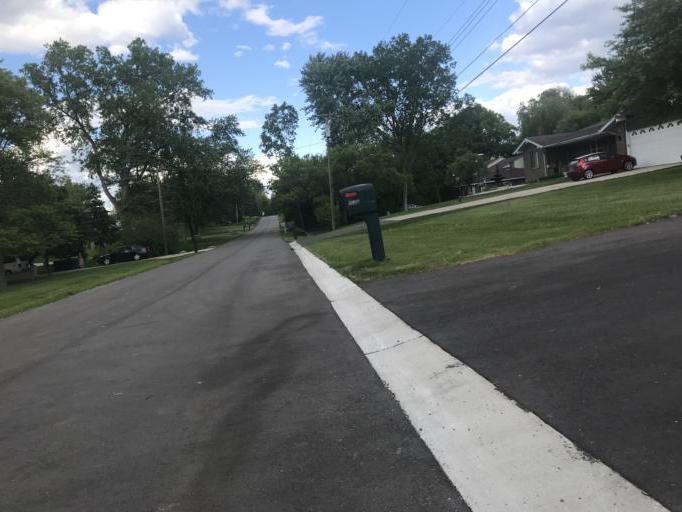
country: US
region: Michigan
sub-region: Oakland County
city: Farmington
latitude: 42.4732
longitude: -83.3423
